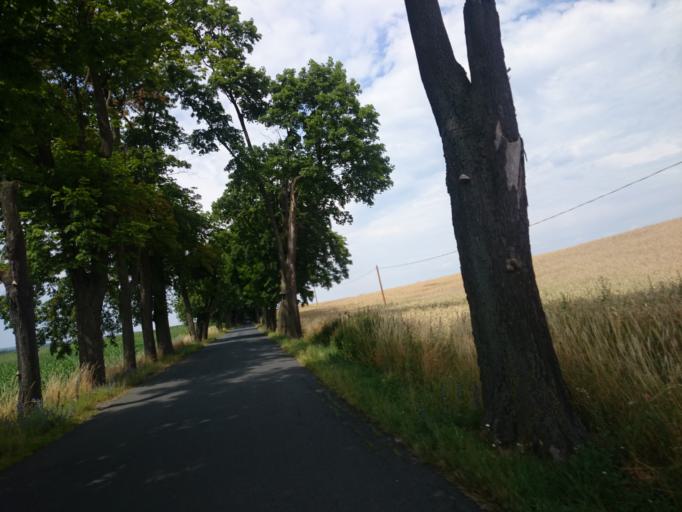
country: PL
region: West Pomeranian Voivodeship
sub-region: Powiat gryfinski
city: Moryn
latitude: 52.9090
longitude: 14.3707
